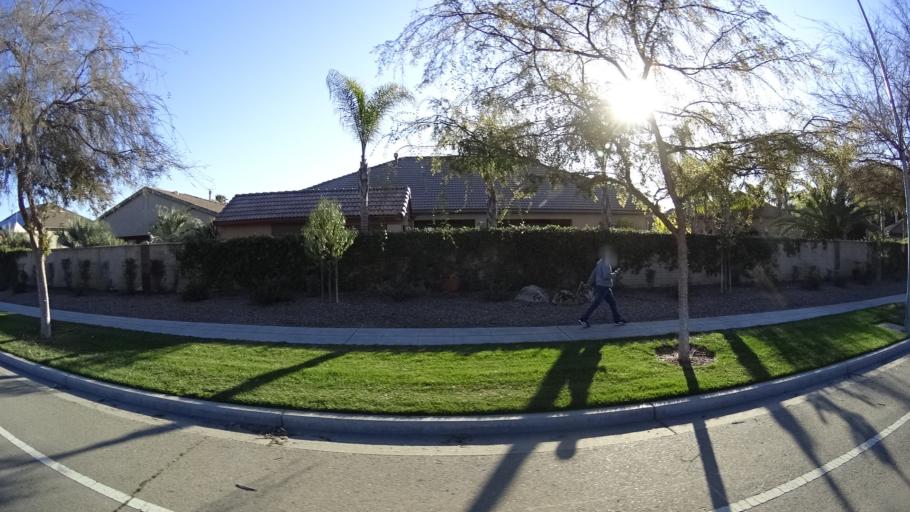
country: US
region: California
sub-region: Fresno County
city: Biola
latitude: 36.8204
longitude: -119.9165
